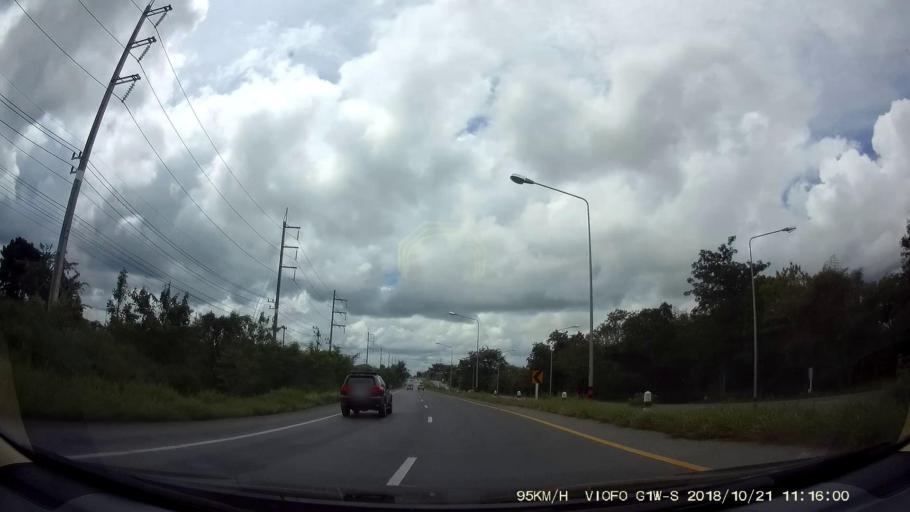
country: TH
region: Chaiyaphum
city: Chaiyaphum
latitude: 15.8901
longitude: 102.1079
